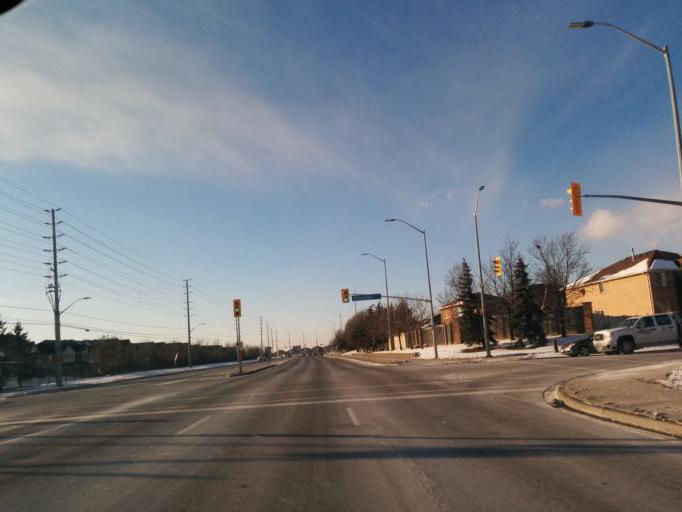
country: CA
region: Ontario
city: Mississauga
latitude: 43.5955
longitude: -79.6749
